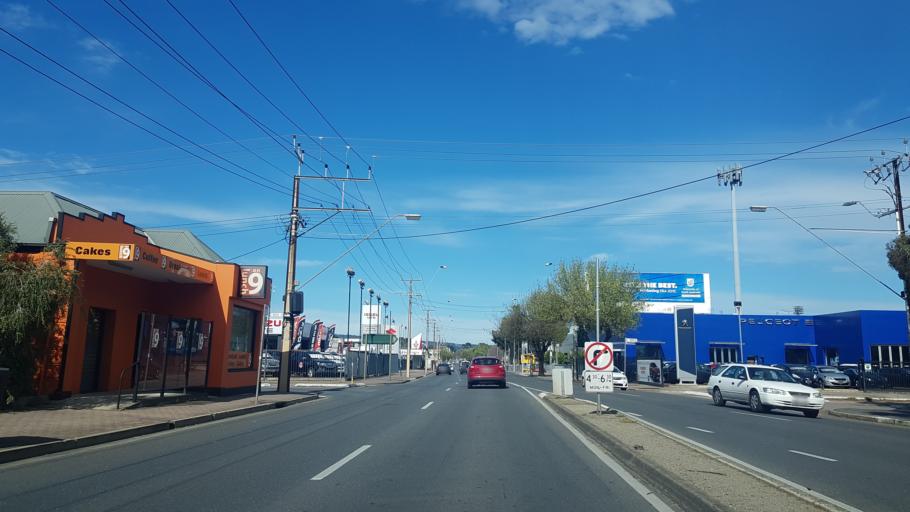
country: AU
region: South Australia
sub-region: Unley
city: Wayville
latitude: -34.9427
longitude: 138.5890
